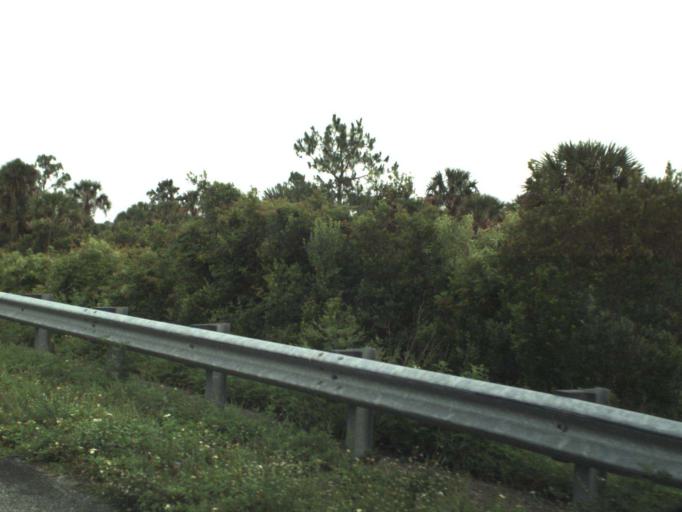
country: US
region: Florida
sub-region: Seminole County
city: Geneva
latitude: 28.6956
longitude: -81.0032
